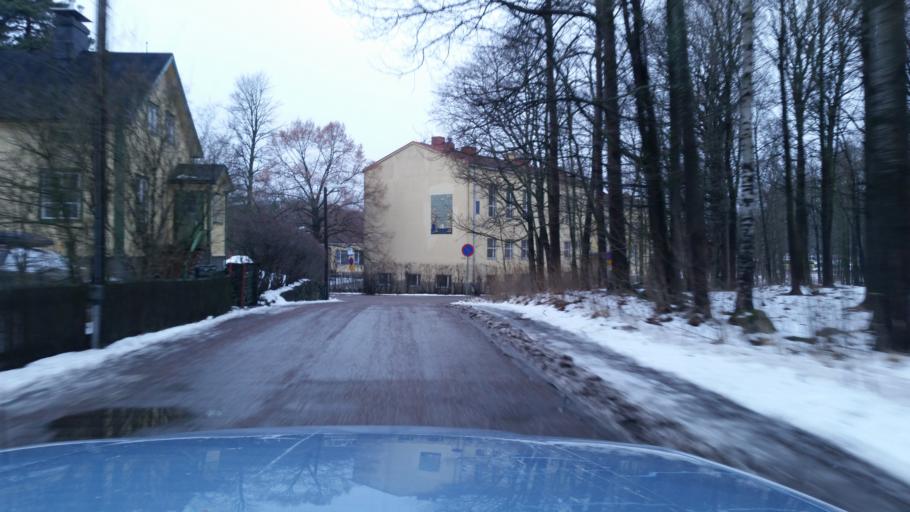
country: FI
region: Uusimaa
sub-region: Helsinki
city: Helsinki
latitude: 60.2112
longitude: 24.9733
